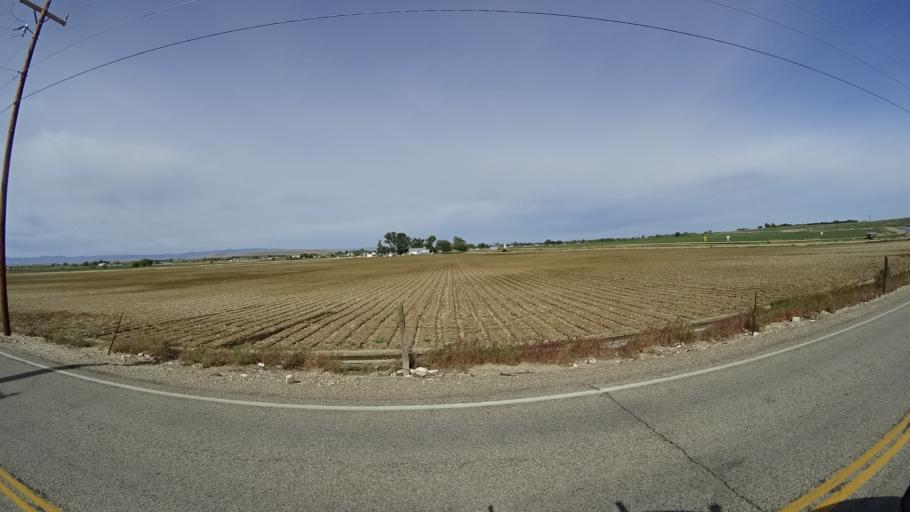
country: US
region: Idaho
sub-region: Ada County
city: Kuna
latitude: 43.4736
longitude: -116.3342
